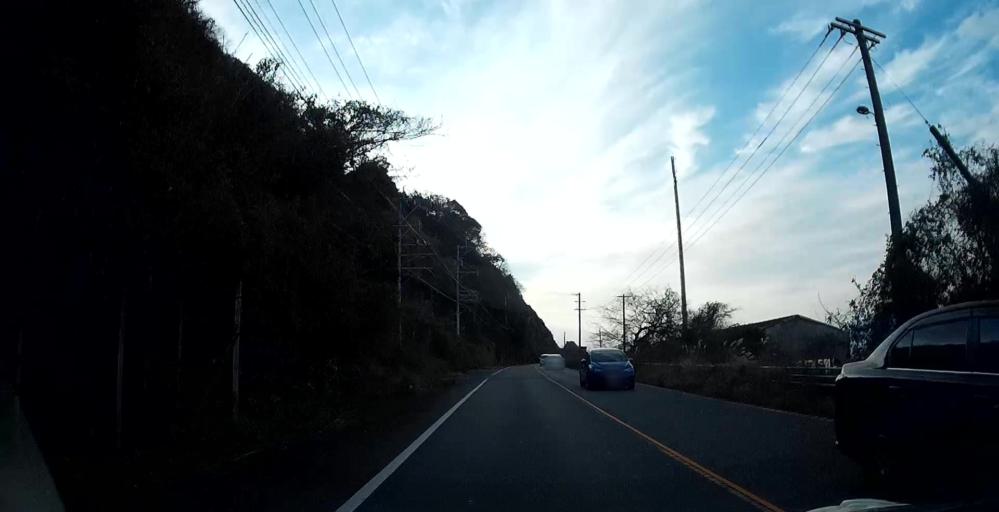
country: JP
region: Nagasaki
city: Shimabara
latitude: 32.6357
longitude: 130.4690
